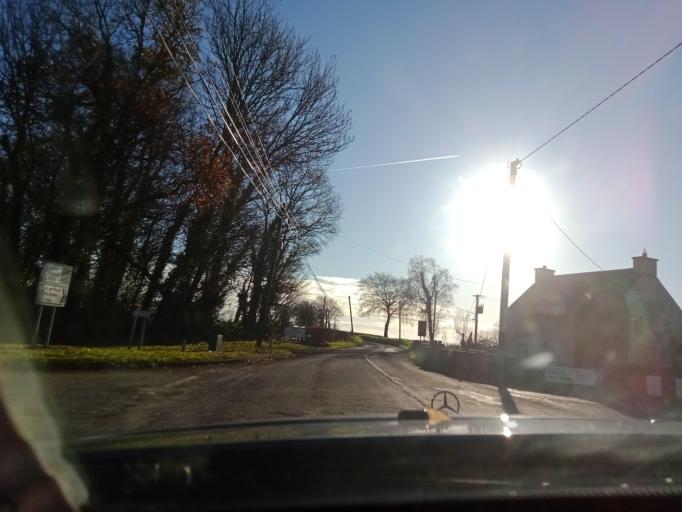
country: IE
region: Leinster
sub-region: Kilkenny
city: Piltown
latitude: 52.3711
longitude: -7.3359
